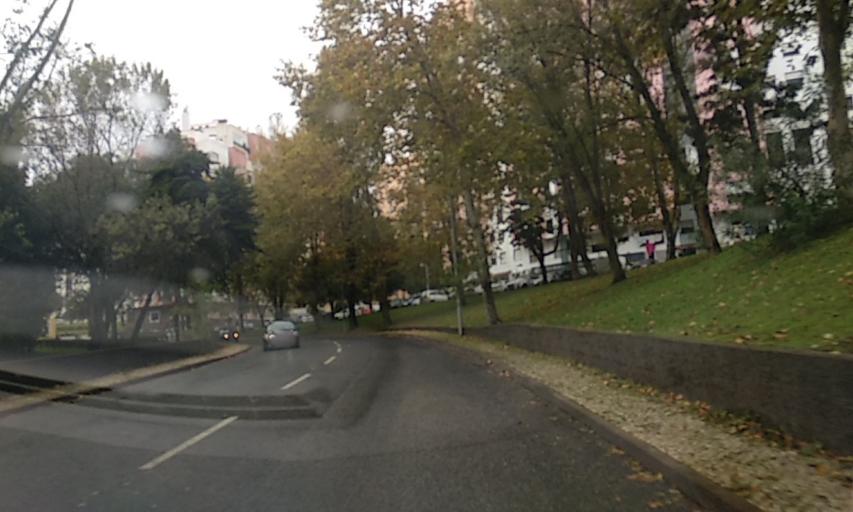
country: PT
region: Lisbon
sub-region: Oeiras
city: Barcarena
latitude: 38.7530
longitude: -9.2805
